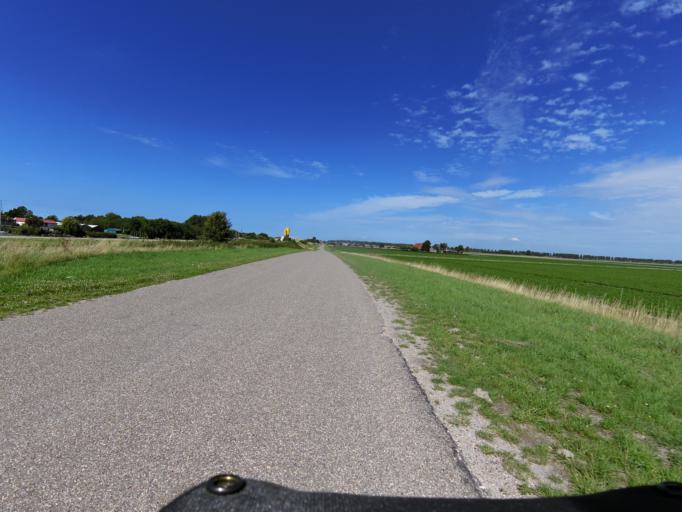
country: NL
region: Zeeland
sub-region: Gemeente Noord-Beveland
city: Kamperland
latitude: 51.5574
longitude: 3.6937
